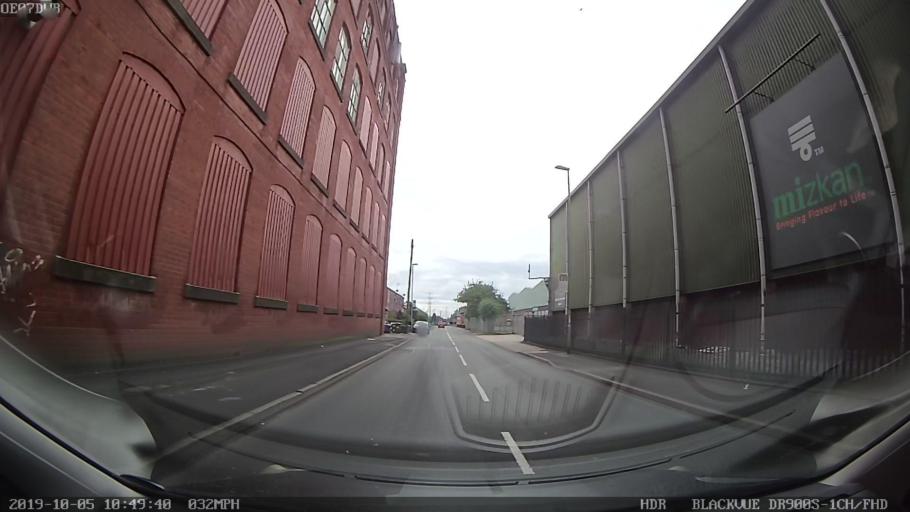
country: GB
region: England
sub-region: Borough of Rochdale
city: Middleton
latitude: 53.5482
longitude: -2.1696
